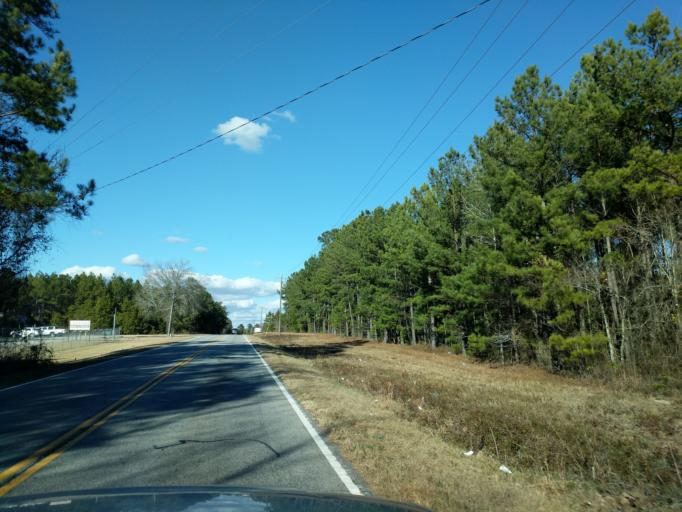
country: US
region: South Carolina
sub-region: Greenwood County
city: Ninety Six
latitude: 34.2889
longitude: -82.0466
